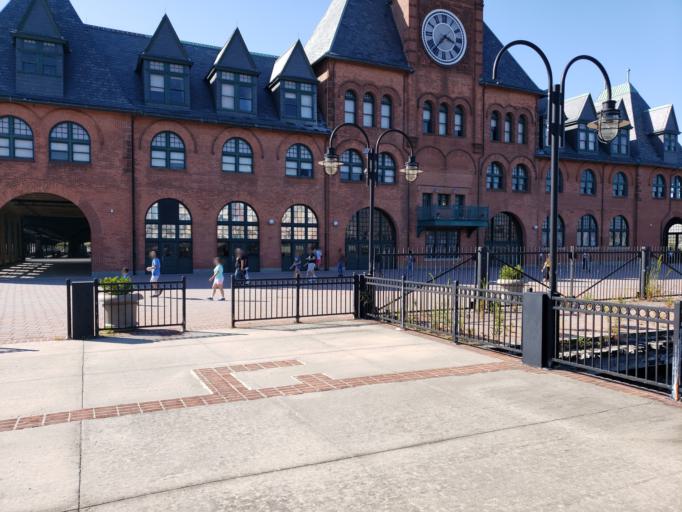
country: US
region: New York
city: New York City
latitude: 40.7070
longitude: -74.0345
